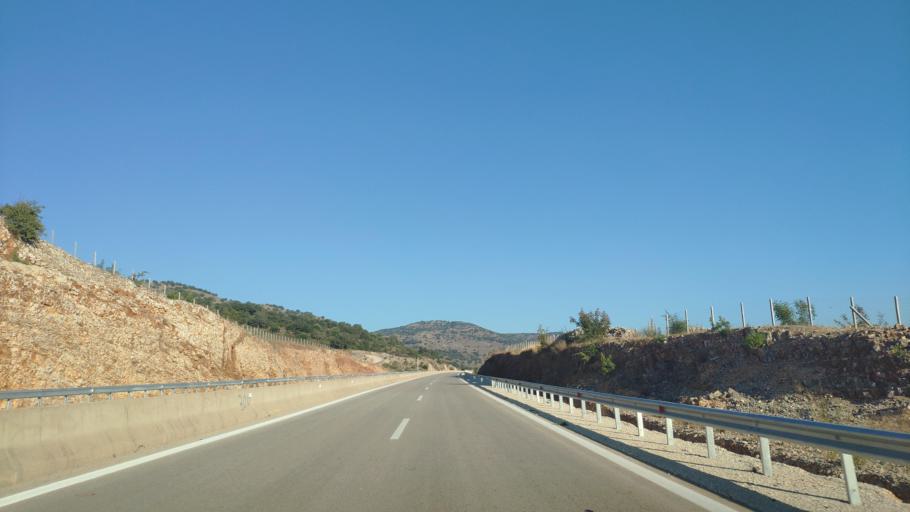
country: GR
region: West Greece
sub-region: Nomos Aitolias kai Akarnanias
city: Katouna
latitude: 38.8477
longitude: 21.0977
